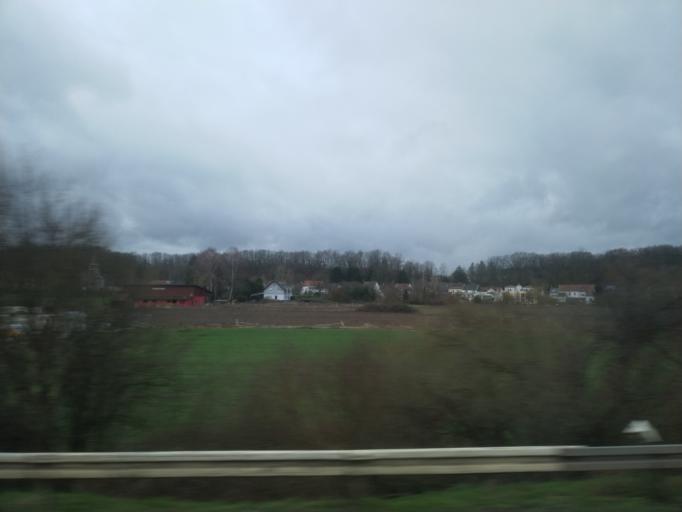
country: DE
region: Saarland
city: Wallerfangen
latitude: 49.3181
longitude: 6.7310
